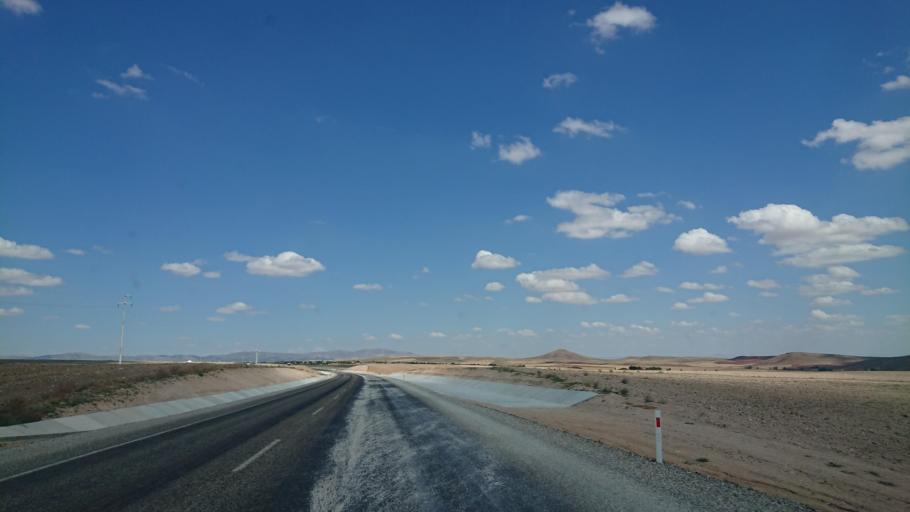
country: TR
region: Kirsehir
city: Kirsehir
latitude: 39.1217
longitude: 34.0110
